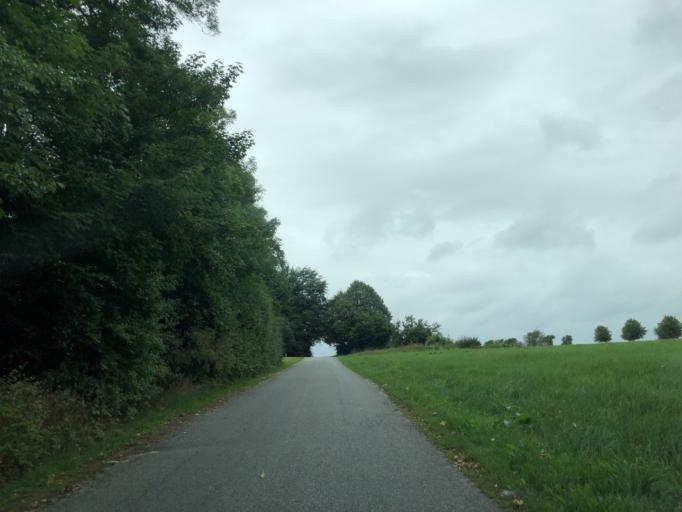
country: DK
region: Central Jutland
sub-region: Herning Kommune
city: Lind
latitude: 56.0842
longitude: 8.9560
